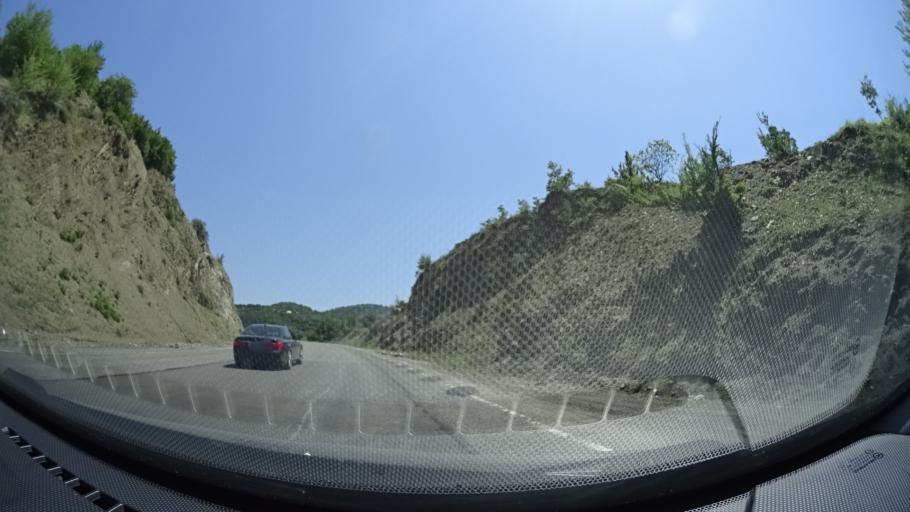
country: GE
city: Zhinvali
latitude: 42.1588
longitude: 44.7044
